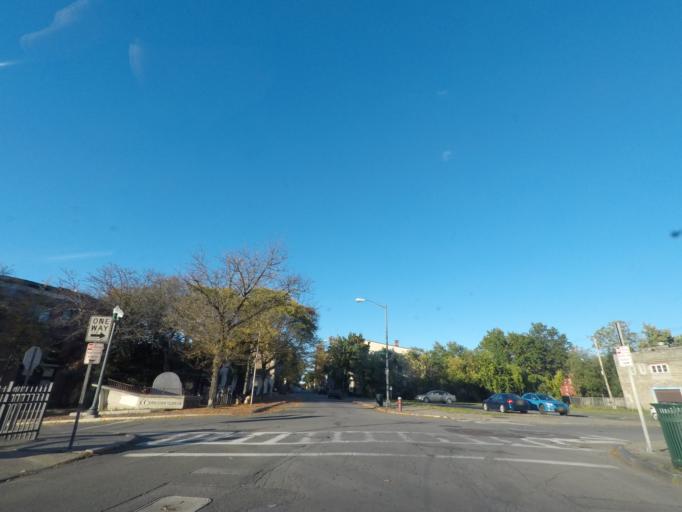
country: US
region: New York
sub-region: Rensselaer County
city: Troy
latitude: 42.7356
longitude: -73.6860
